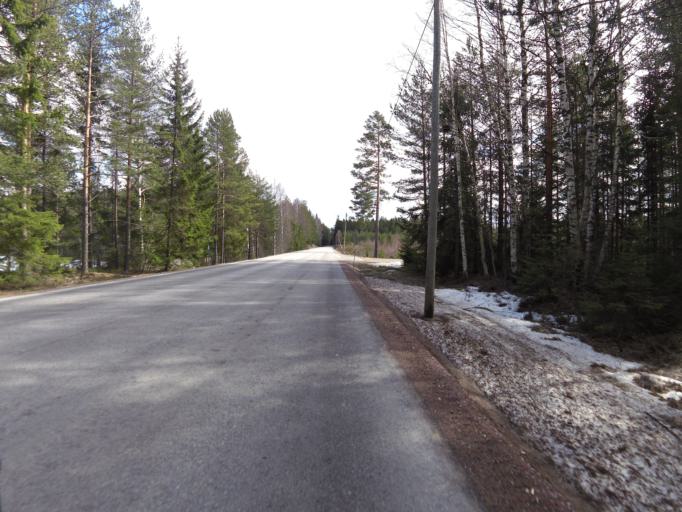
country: SE
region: Dalarna
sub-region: Hedemora Kommun
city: Brunna
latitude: 60.3149
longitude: 16.1431
